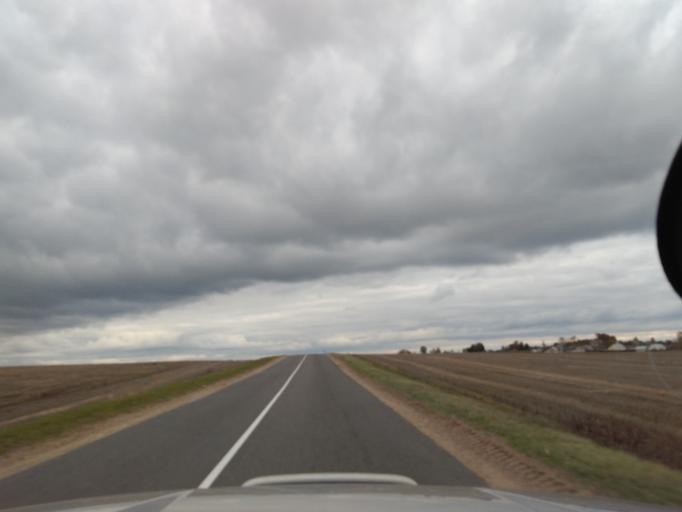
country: BY
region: Minsk
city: Slutsk
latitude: 53.1965
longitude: 27.3570
